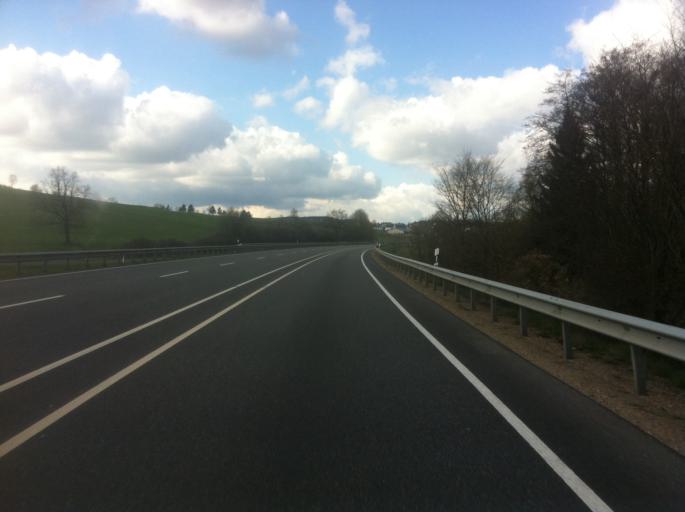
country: DE
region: Rheinland-Pfalz
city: Olzheim
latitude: 50.2614
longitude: 6.4552
